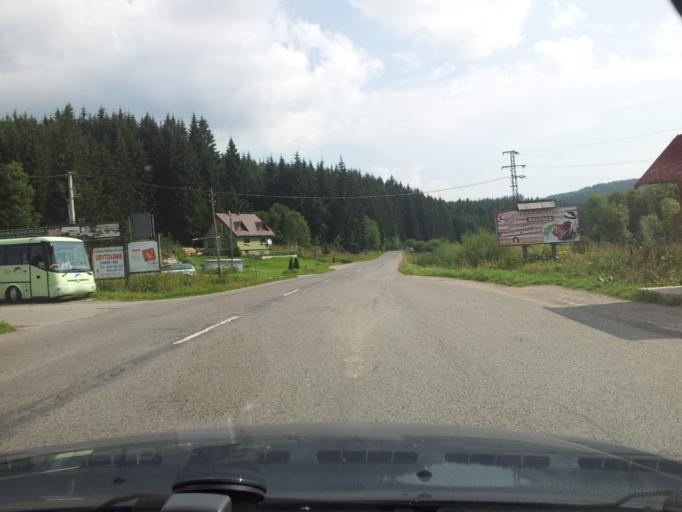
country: SK
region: Zilinsky
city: Oravska Lesna
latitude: 49.3815
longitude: 19.2231
